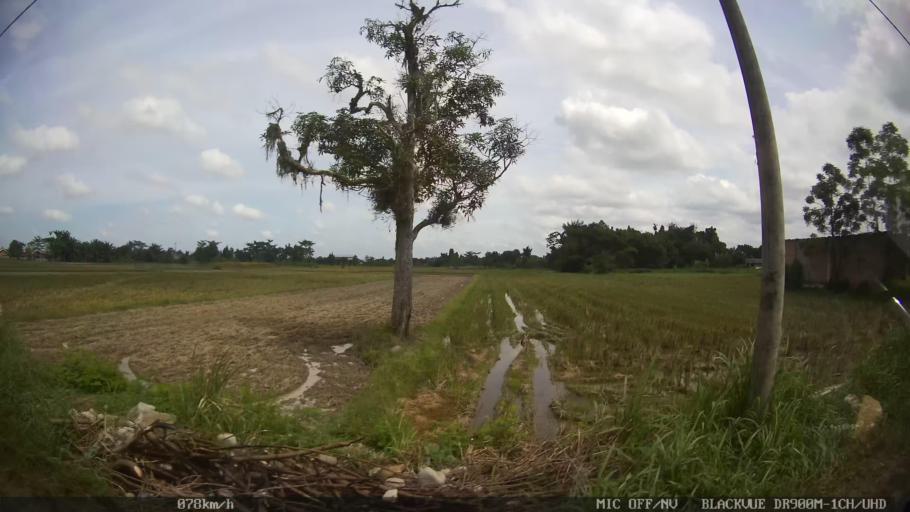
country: ID
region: North Sumatra
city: Percut
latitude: 3.6094
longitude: 98.8443
